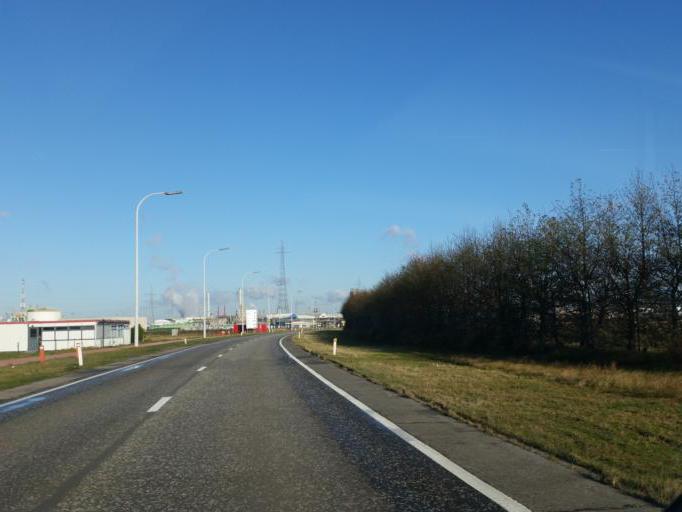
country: BE
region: Flanders
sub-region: Provincie Antwerpen
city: Zwijndrecht
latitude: 51.2333
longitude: 4.3267
